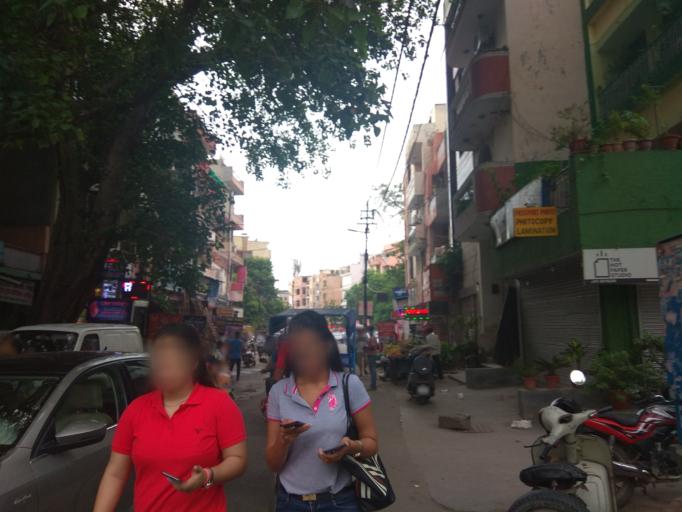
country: IN
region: NCT
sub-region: New Delhi
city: New Delhi
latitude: 28.5712
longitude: 77.2428
